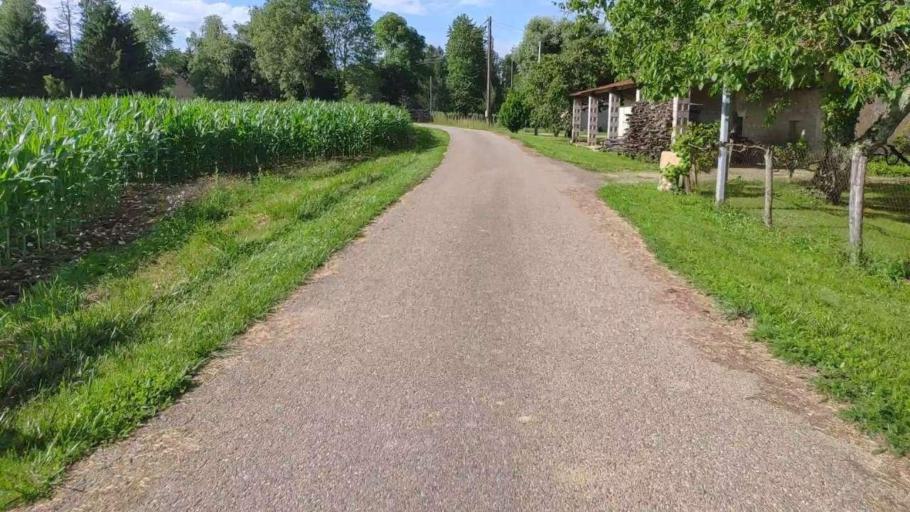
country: FR
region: Franche-Comte
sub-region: Departement du Jura
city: Bletterans
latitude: 46.8126
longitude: 5.4960
